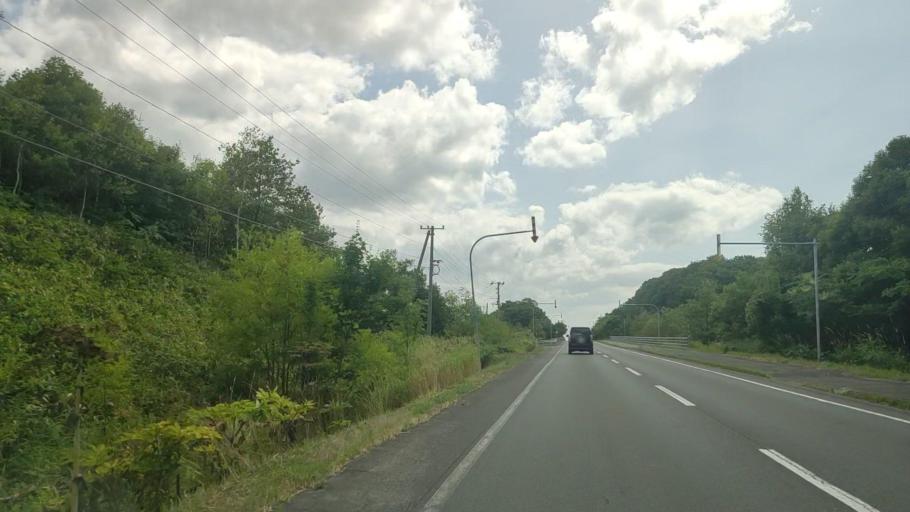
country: JP
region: Hokkaido
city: Makubetsu
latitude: 44.7665
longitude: 141.7932
